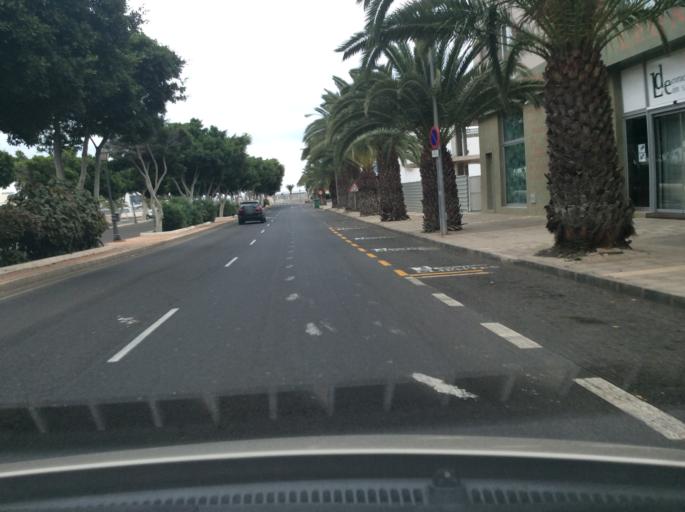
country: ES
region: Canary Islands
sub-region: Provincia de Las Palmas
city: Arrecife
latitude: 28.9664
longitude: -13.5422
